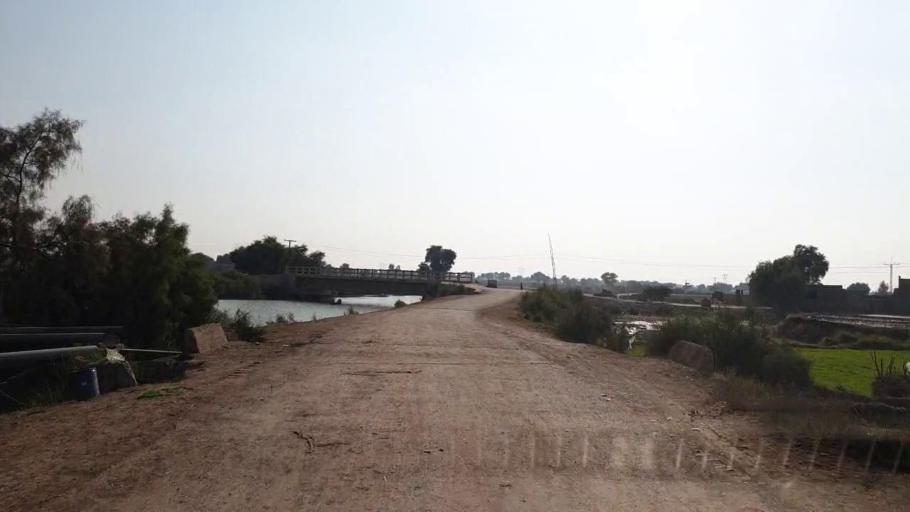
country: PK
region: Sindh
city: Sehwan
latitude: 26.4432
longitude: 67.8095
